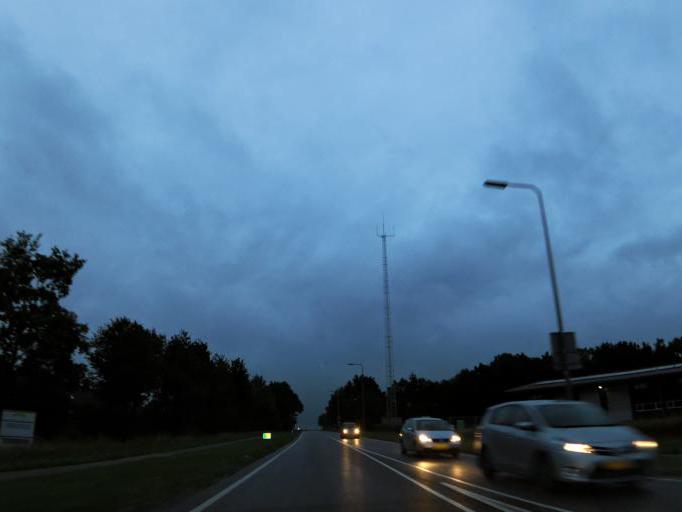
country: NL
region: Limburg
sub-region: Gemeente Onderbanken
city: Schinveld
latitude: 50.9661
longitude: 5.9725
